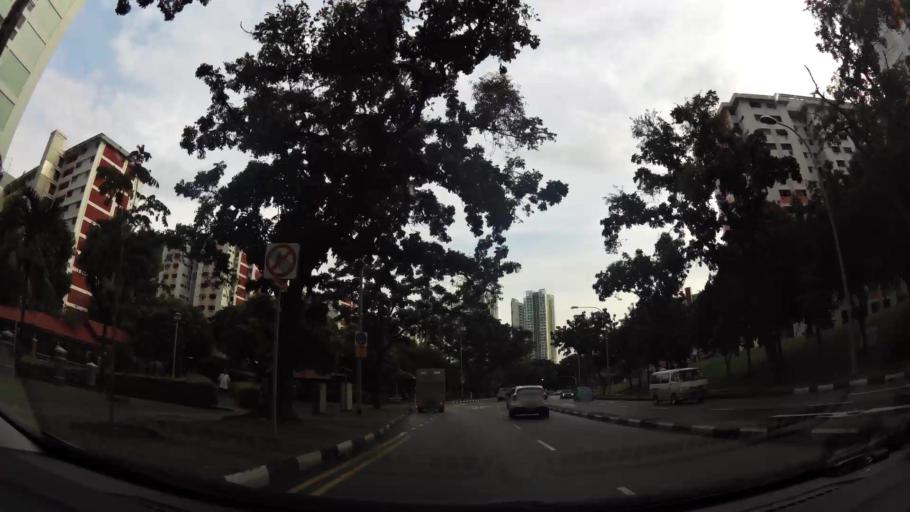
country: SG
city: Singapore
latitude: 1.3721
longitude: 103.8565
